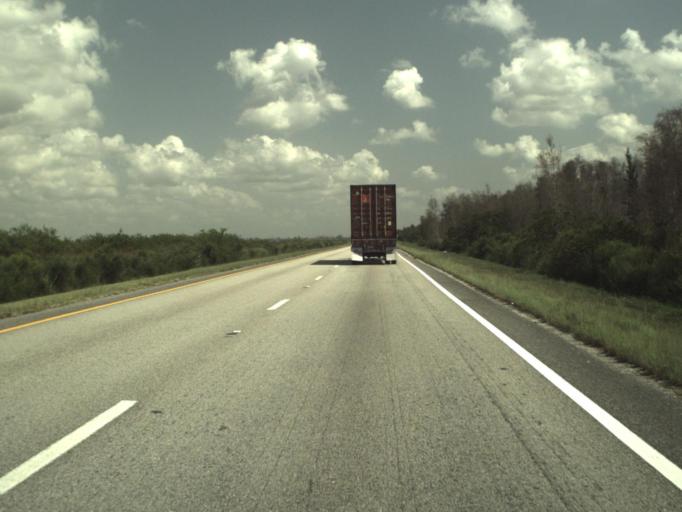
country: US
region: Florida
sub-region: Miami-Dade County
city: Palm Springs North
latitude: 25.9741
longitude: -80.4313
